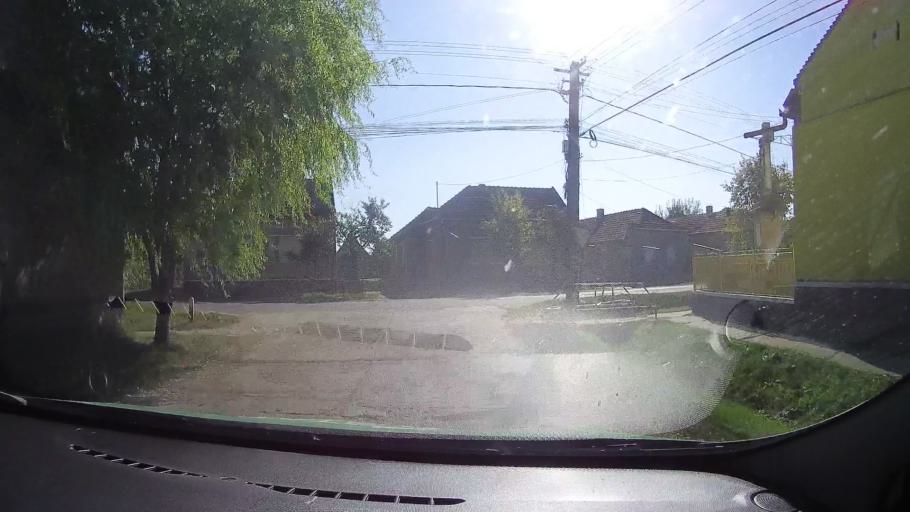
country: RO
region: Satu Mare
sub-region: Comuna Capleni
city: Capleni
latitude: 47.7059
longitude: 22.4984
